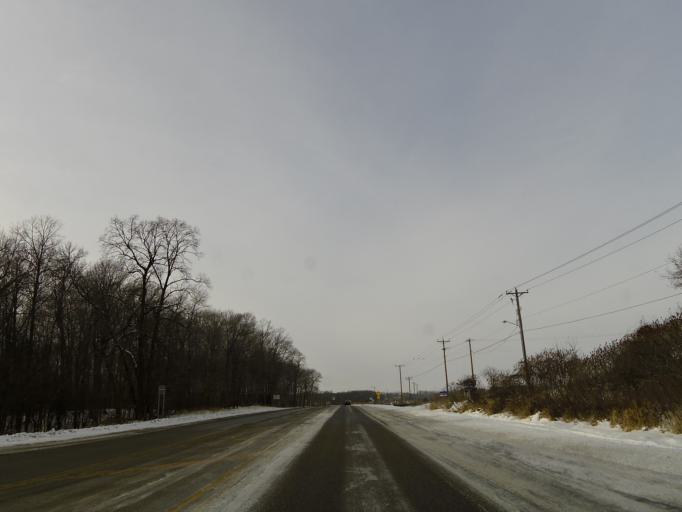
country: US
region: Minnesota
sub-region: Hennepin County
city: Saint Bonifacius
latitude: 44.8911
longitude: -93.7006
